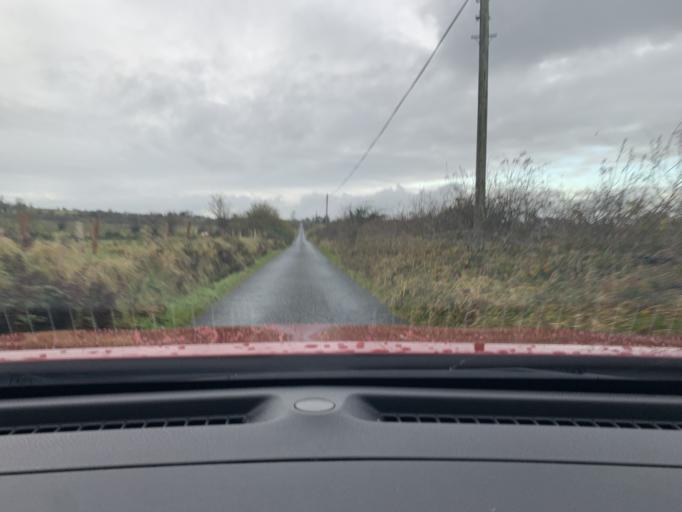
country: IE
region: Connaught
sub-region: Roscommon
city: Ballaghaderreen
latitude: 53.9650
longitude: -8.5450
